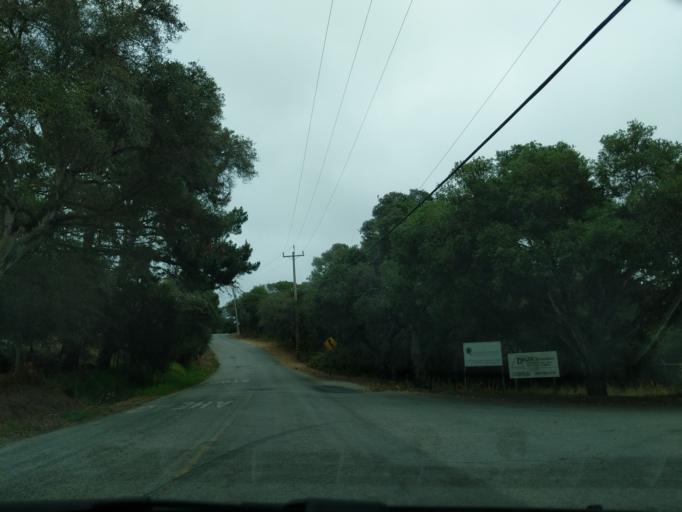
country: US
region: California
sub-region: Monterey County
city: Prunedale
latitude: 36.7889
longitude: -121.7007
